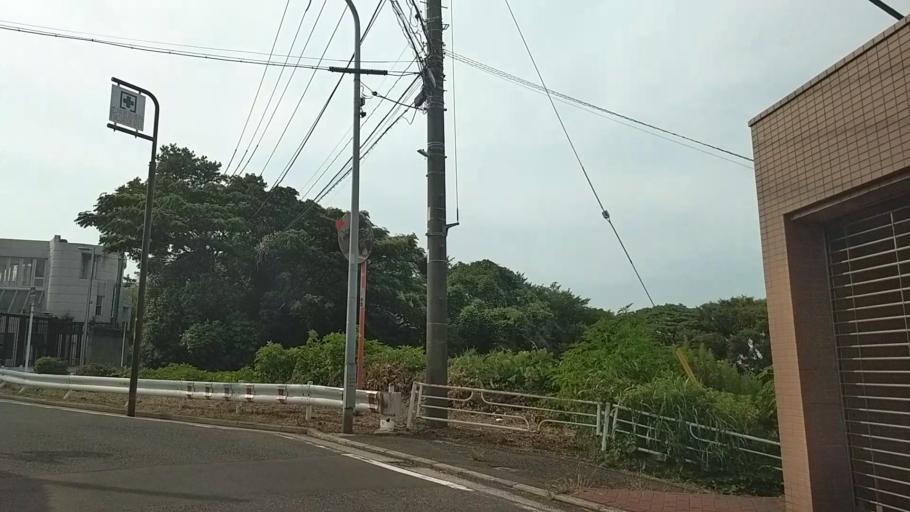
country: JP
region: Kanagawa
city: Yokohama
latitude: 35.4343
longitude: 139.6606
